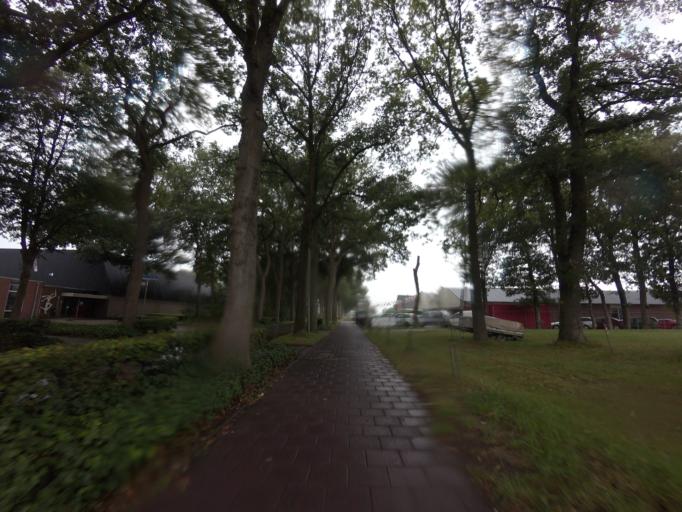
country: NL
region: Drenthe
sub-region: Gemeente Hoogeveen
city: Hoogeveen
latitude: 52.6681
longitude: 6.4977
